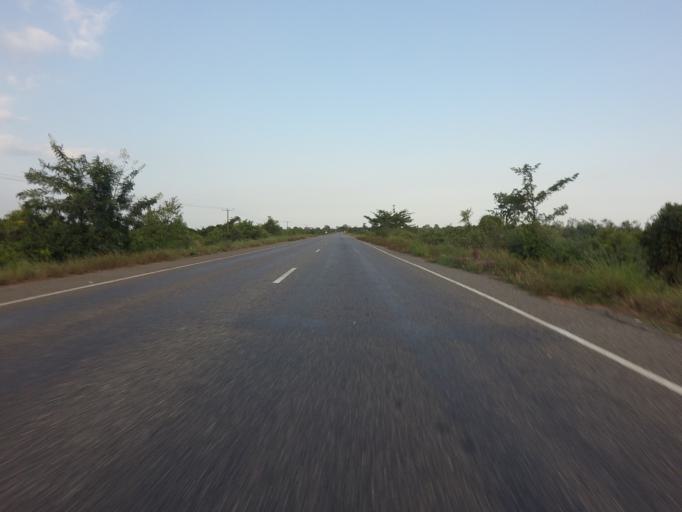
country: GH
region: Volta
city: Anloga
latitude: 6.0766
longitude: 0.5982
